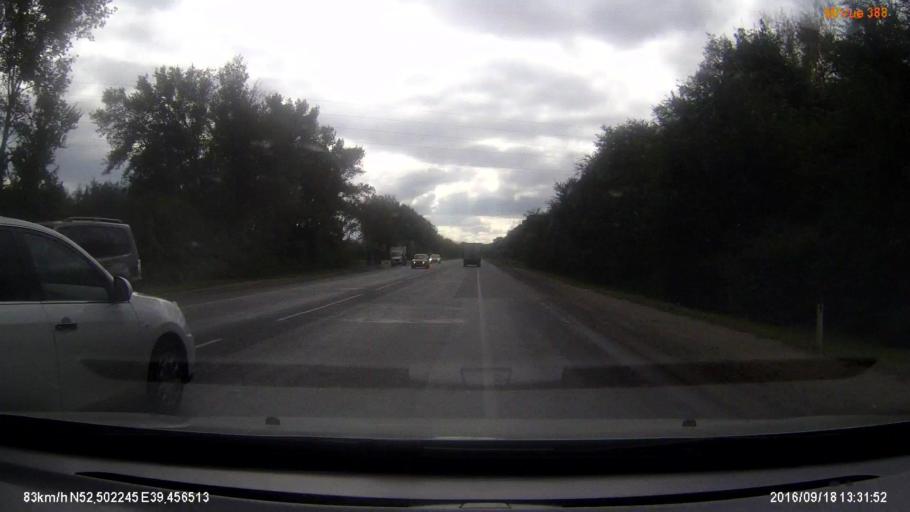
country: RU
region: Lipetsk
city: Borinskoye
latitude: 52.4665
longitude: 39.4101
